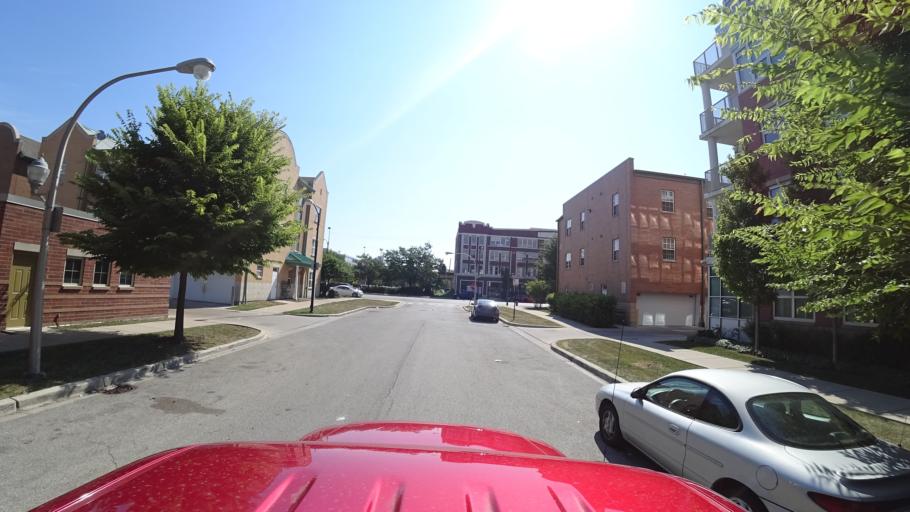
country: US
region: Illinois
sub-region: Cook County
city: Chicago
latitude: 41.8291
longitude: -87.6273
